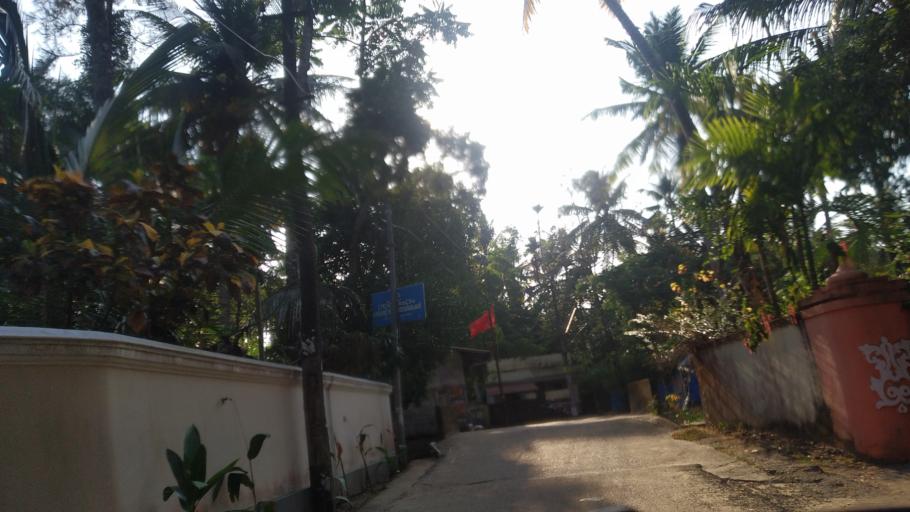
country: IN
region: Kerala
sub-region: Thrissur District
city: Kodungallur
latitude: 10.1302
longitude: 76.2028
